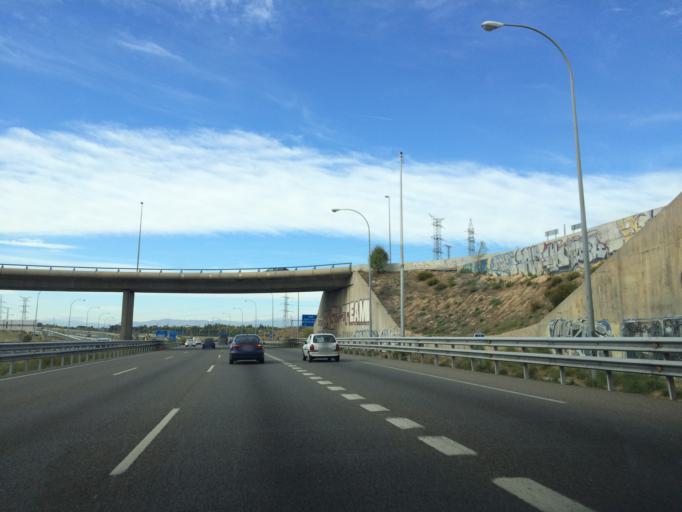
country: ES
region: Madrid
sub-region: Provincia de Madrid
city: Las Tablas
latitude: 40.5159
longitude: -3.6701
